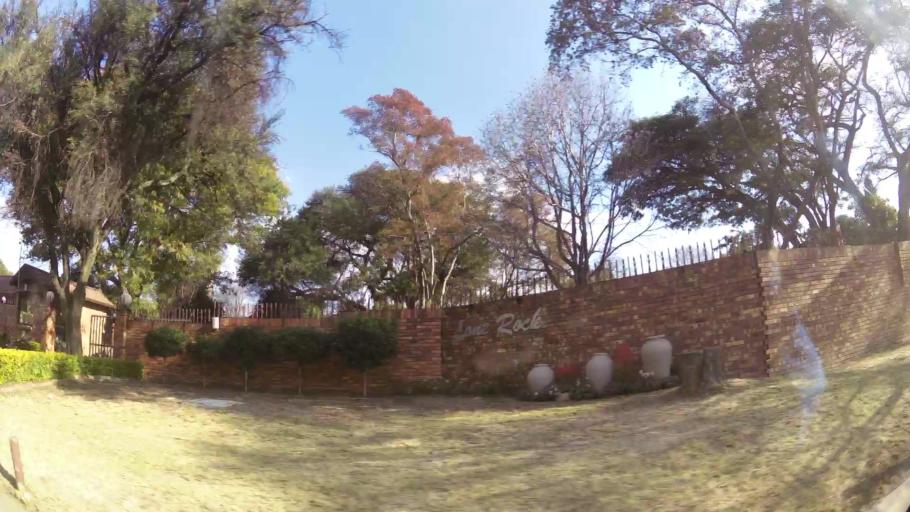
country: ZA
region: Gauteng
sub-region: City of Johannesburg Metropolitan Municipality
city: Diepsloot
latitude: -26.0177
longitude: 28.0290
